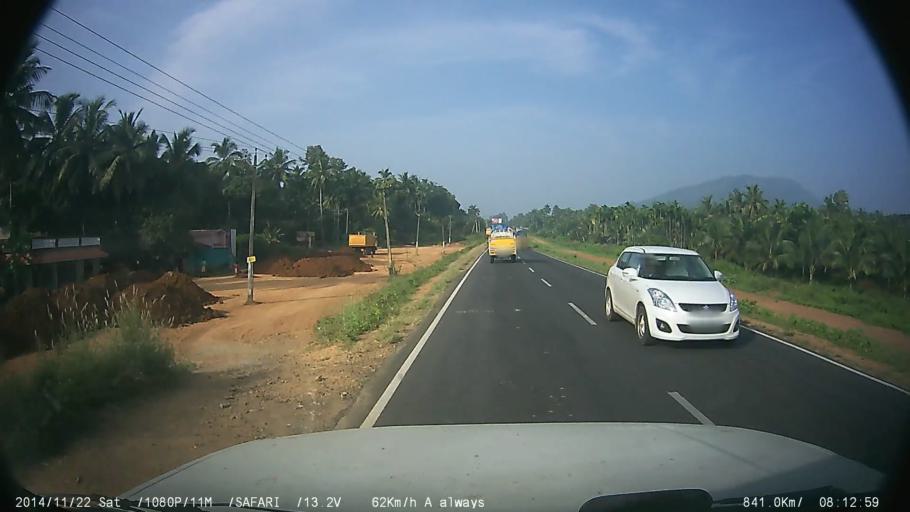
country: IN
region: Kerala
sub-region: Thrissur District
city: Chelakara
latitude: 10.5820
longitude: 76.4279
